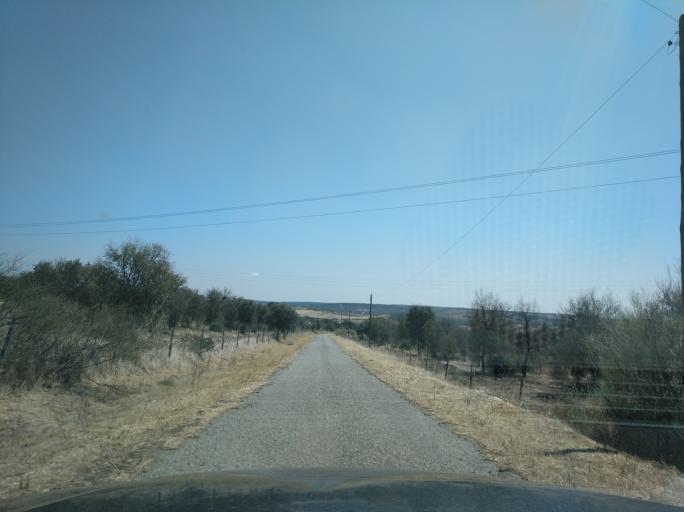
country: PT
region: Portalegre
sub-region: Campo Maior
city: Campo Maior
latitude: 39.0018
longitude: -7.0927
